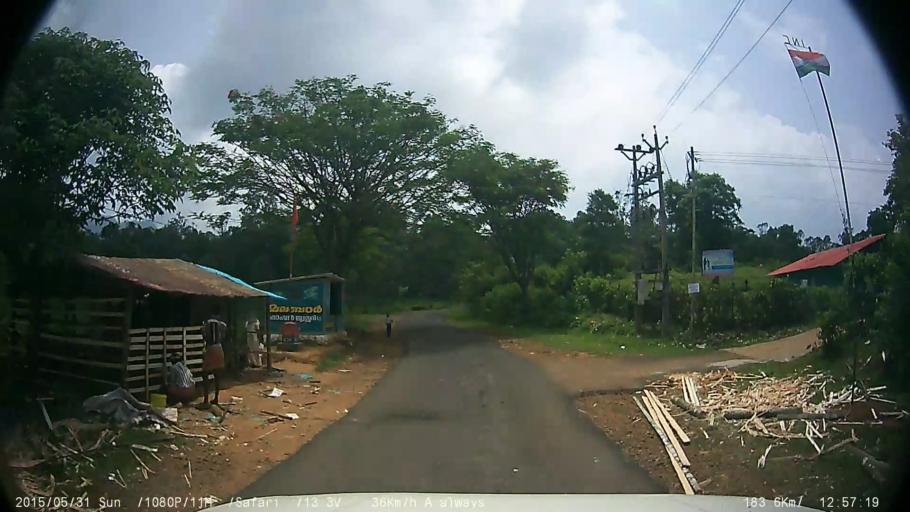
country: IN
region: Kerala
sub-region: Wayanad
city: Kalpetta
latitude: 11.5090
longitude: 76.1427
